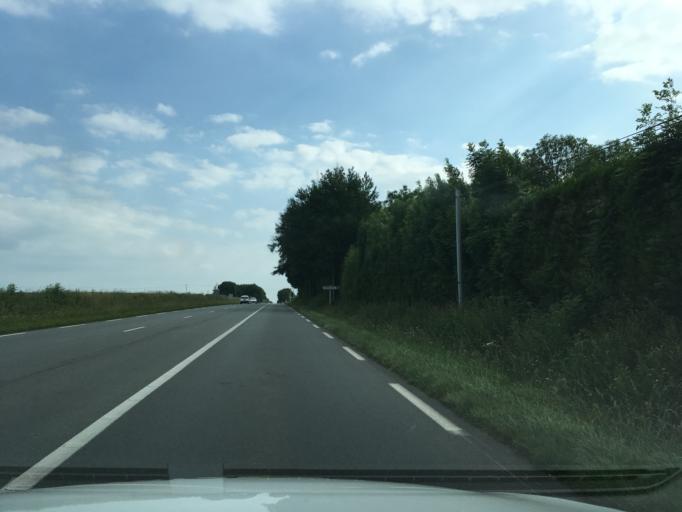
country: FR
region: Poitou-Charentes
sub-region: Departement des Deux-Sevres
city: Le Tallud
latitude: 46.6152
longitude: -0.2836
